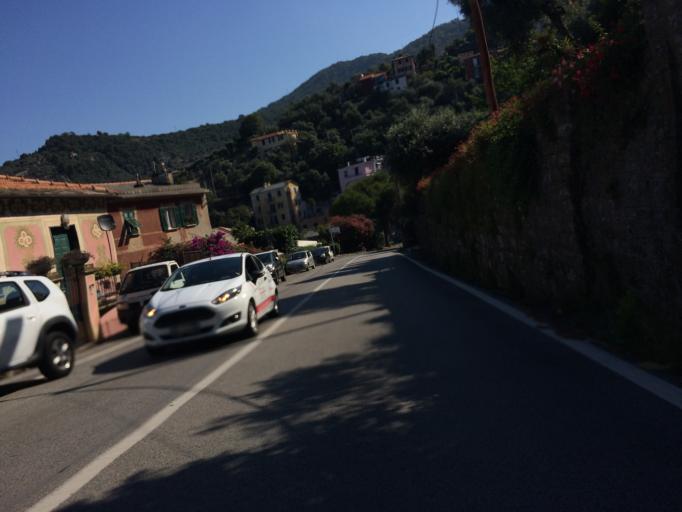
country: IT
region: Liguria
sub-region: Provincia di Genova
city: Camogli
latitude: 44.3548
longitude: 9.1543
